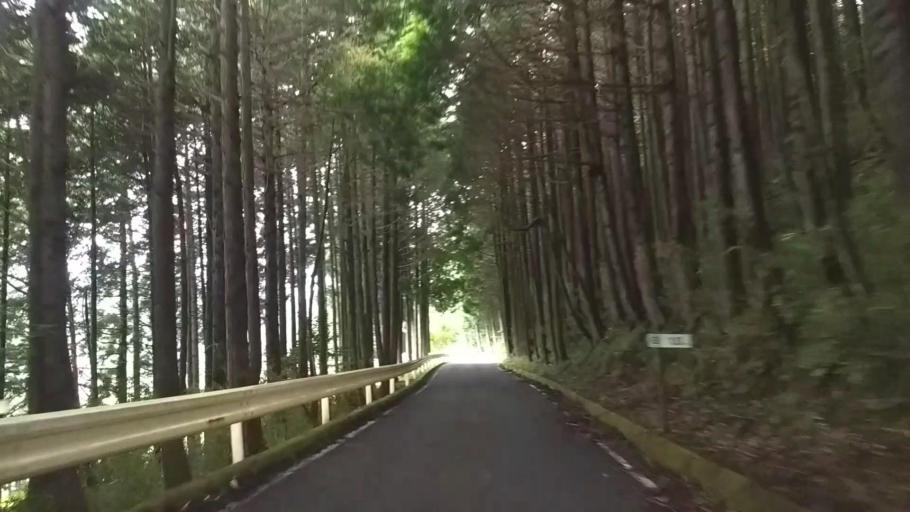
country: JP
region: Shizuoka
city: Gotemba
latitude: 35.3264
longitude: 138.9867
